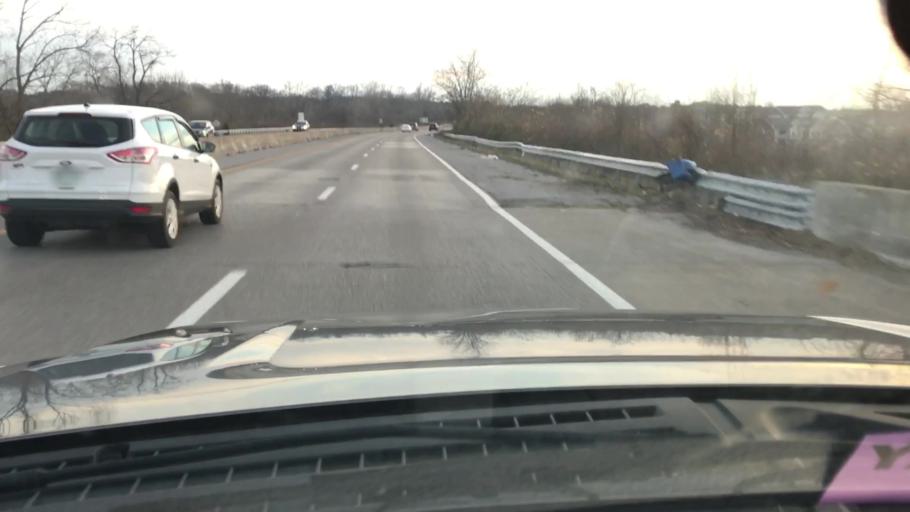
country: US
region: Tennessee
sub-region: Wilson County
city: Green Hill
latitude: 36.1738
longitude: -86.6061
